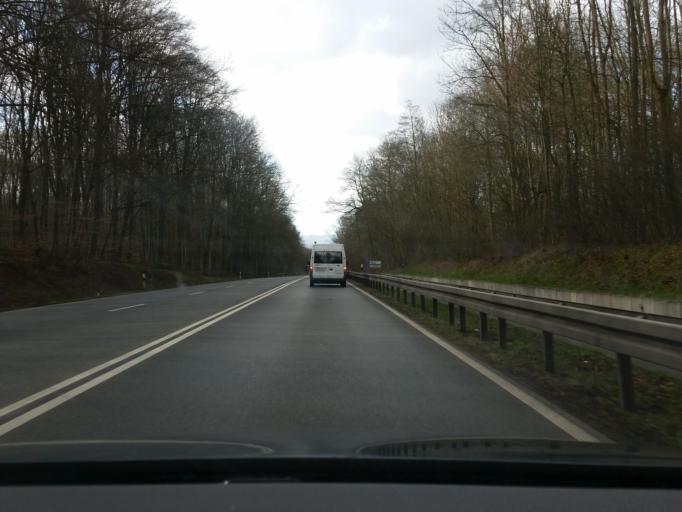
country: DE
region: Hesse
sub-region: Regierungsbezirk Giessen
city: Alten Buseck
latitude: 50.5641
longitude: 8.7417
